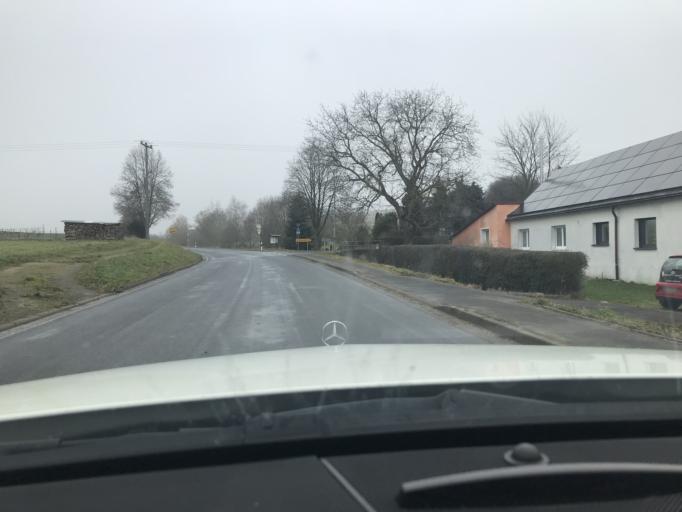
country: DE
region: Bavaria
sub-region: Regierungsbezirk Unterfranken
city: Werneck
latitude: 50.0036
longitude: 10.0640
